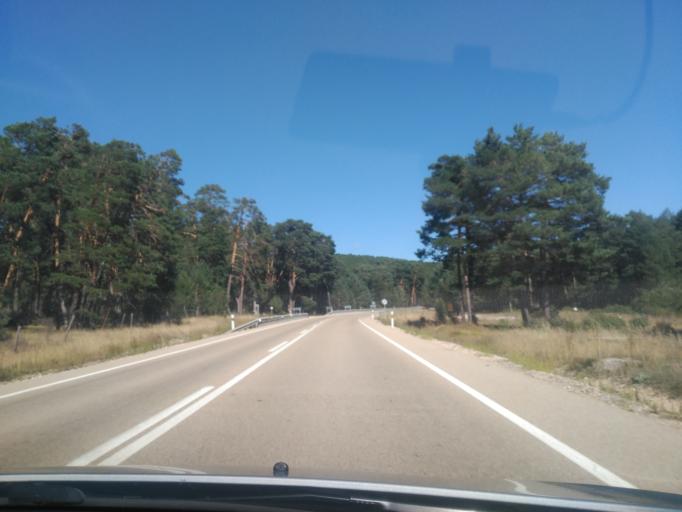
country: ES
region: Castille and Leon
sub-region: Provincia de Soria
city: Navaleno
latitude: 41.8386
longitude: -3.0305
